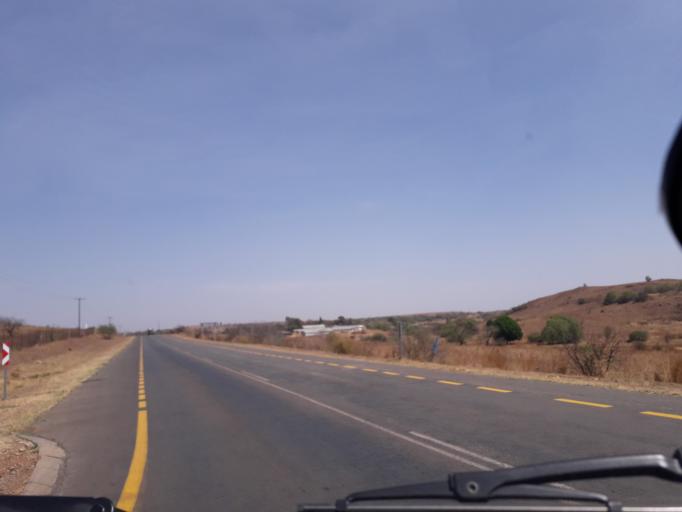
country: ZA
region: Gauteng
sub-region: West Rand District Municipality
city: Krugersdorp
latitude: -26.0174
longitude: 27.7291
